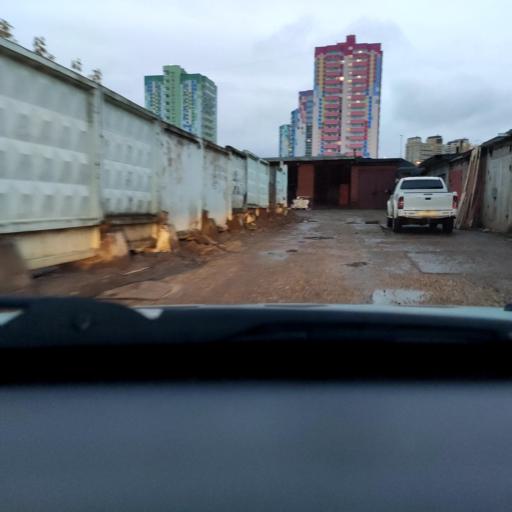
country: RU
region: Perm
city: Perm
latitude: 58.0015
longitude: 56.2007
